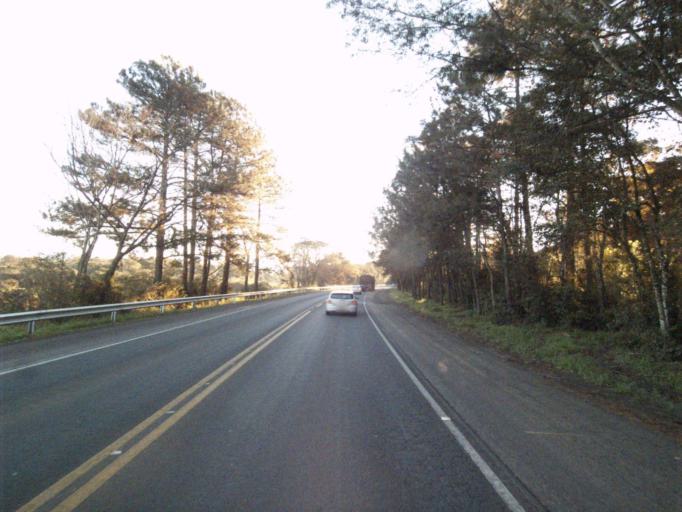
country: BR
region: Santa Catarina
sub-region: Sao Lourenco Do Oeste
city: Sao Lourenco dOeste
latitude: -26.8276
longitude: -53.0799
